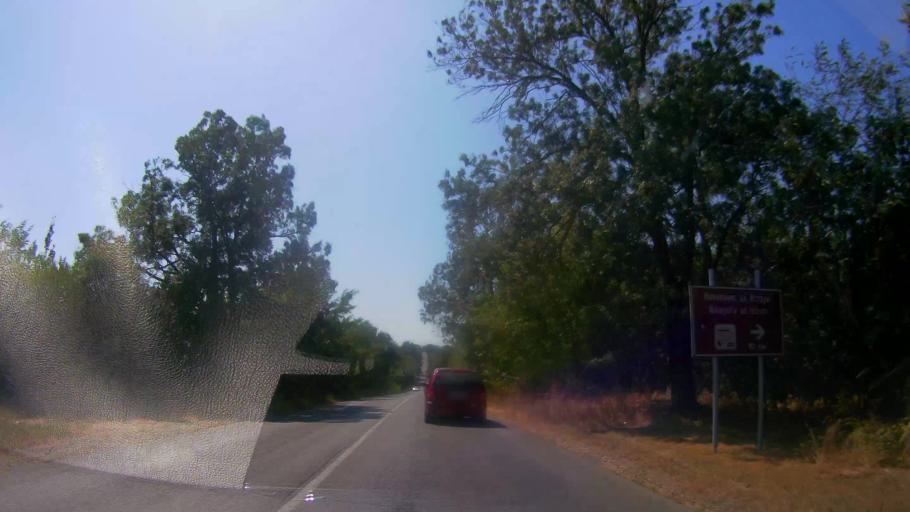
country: BG
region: Veliko Turnovo
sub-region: Obshtina Gorna Oryakhovitsa
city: Purvomaytsi
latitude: 43.2440
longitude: 25.6435
